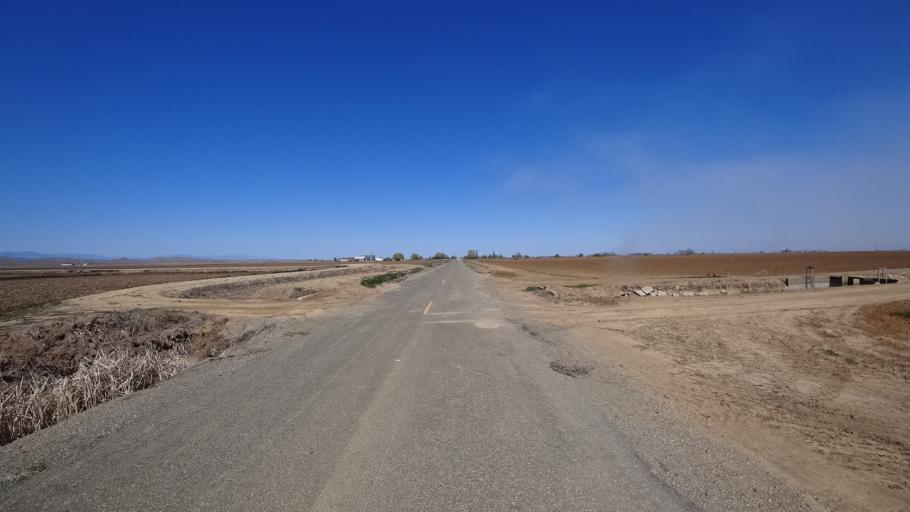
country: US
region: California
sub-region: Colusa County
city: Maxwell
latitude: 39.3879
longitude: -122.2483
